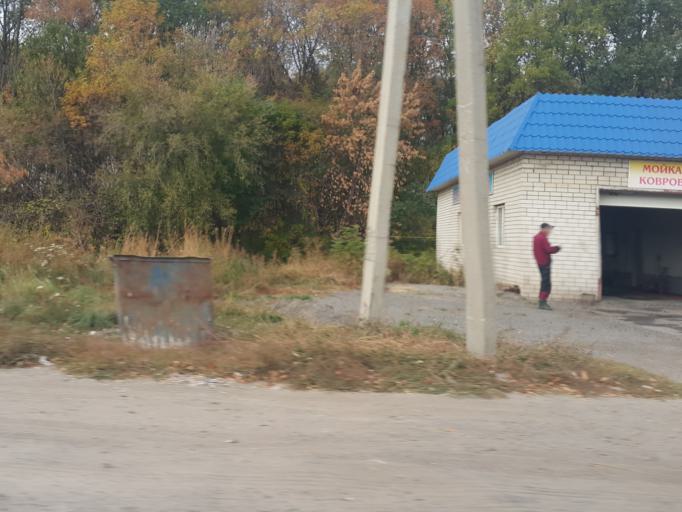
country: RU
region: Tambov
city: Bokino
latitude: 52.6426
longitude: 41.4410
